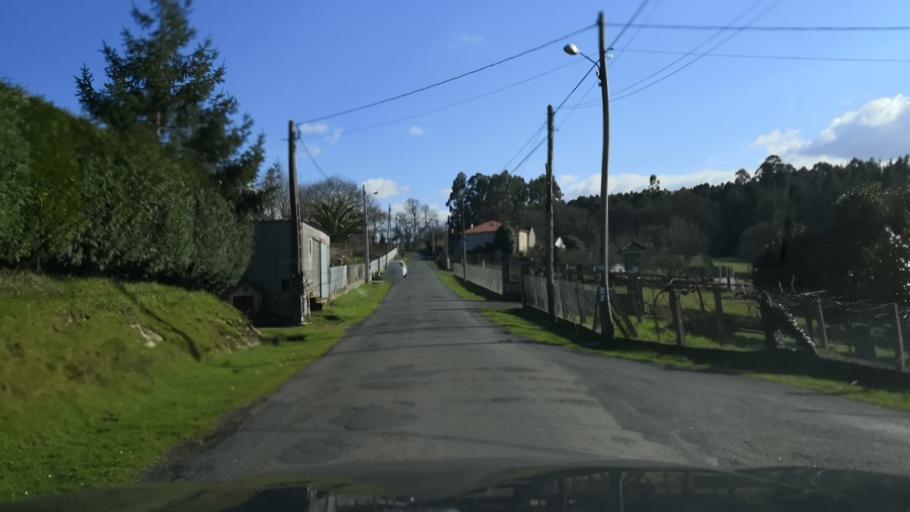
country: ES
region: Galicia
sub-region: Provincia da Coruna
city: Ribeira
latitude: 42.7056
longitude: -8.4282
